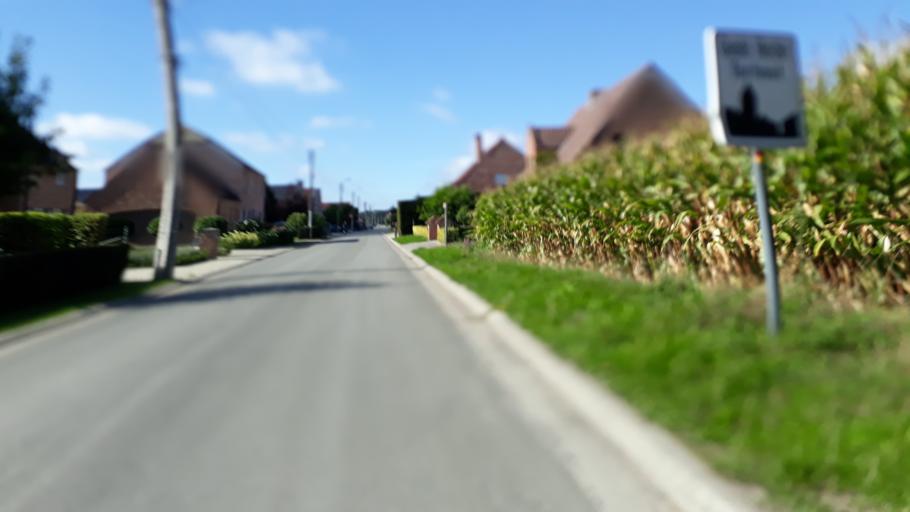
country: BE
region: Flanders
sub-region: Provincie West-Vlaanderen
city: Torhout
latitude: 51.0579
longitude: 3.1213
